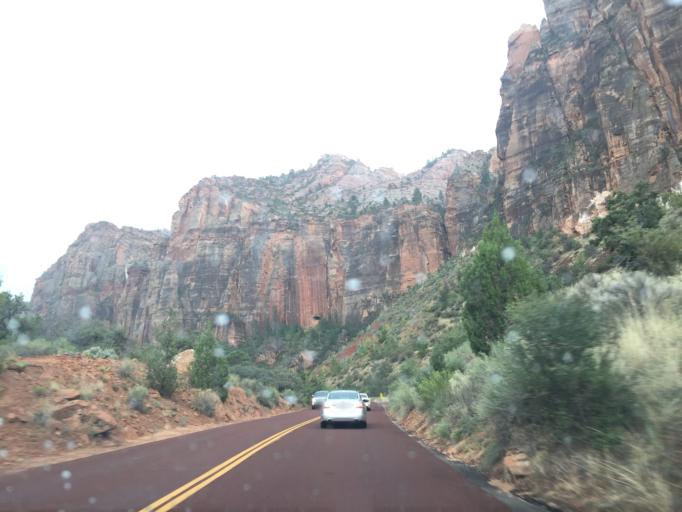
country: US
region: Utah
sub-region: Washington County
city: Hildale
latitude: 37.2139
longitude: -112.9599
